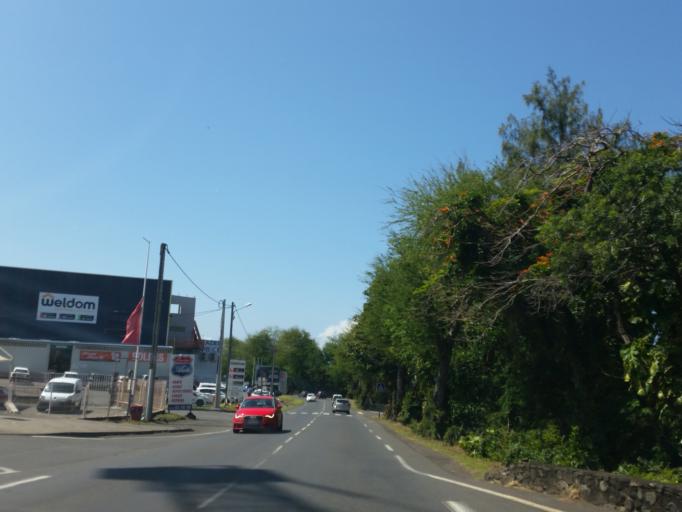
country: RE
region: Reunion
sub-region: Reunion
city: Saint-Joseph
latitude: -21.3795
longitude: 55.6062
